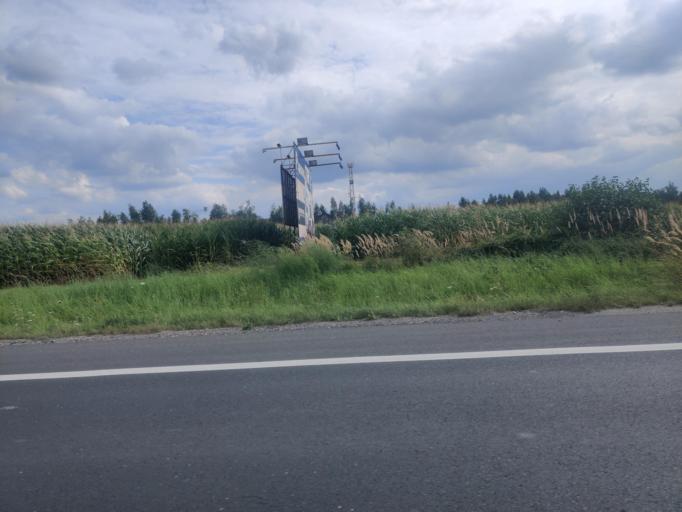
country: PL
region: Greater Poland Voivodeship
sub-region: Powiat koninski
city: Stare Miasto
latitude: 52.1891
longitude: 18.2435
